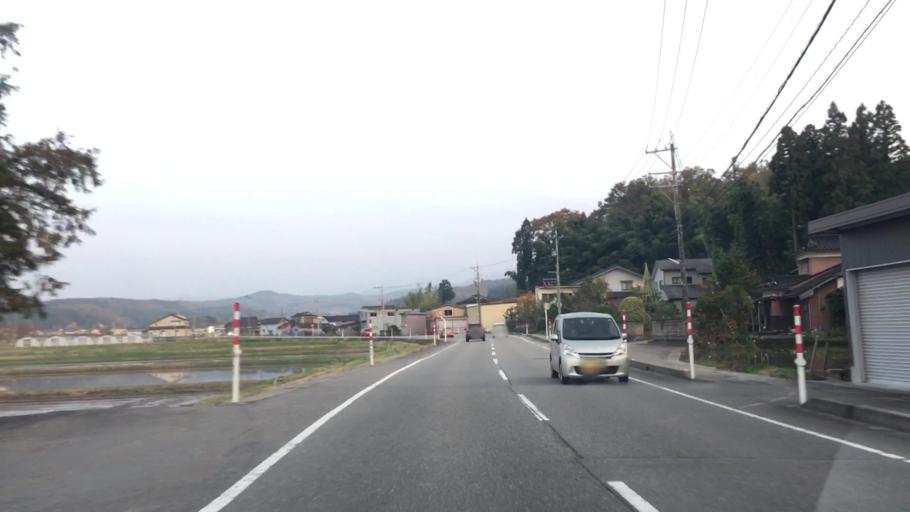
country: JP
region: Toyama
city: Toyama-shi
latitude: 36.6021
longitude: 137.2425
